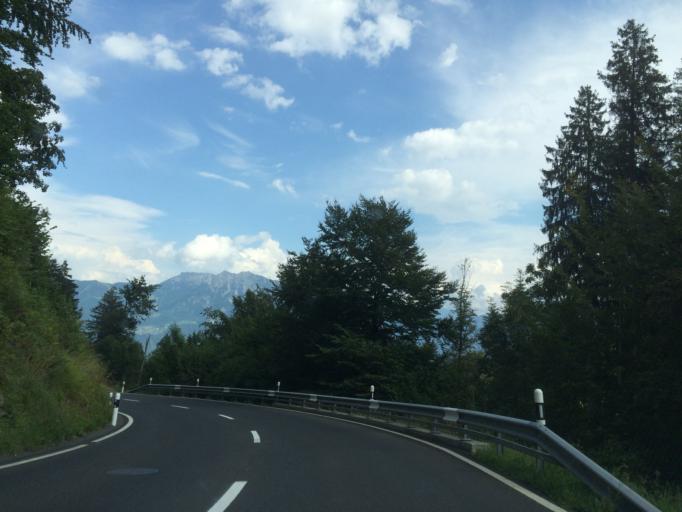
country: CH
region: Saint Gallen
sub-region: Wahlkreis Werdenberg
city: Gams
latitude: 47.1963
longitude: 9.4121
